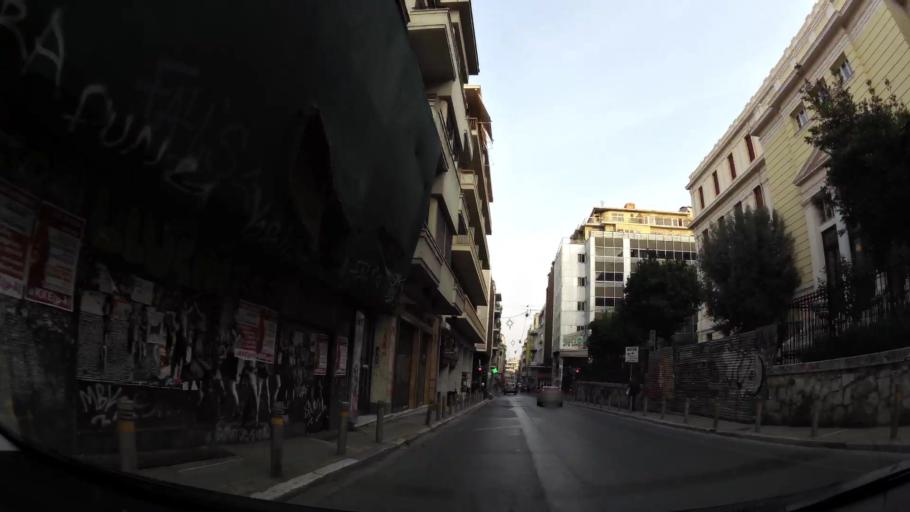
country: GR
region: Attica
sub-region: Nomarchia Athinas
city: Athens
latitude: 37.9831
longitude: 23.7346
